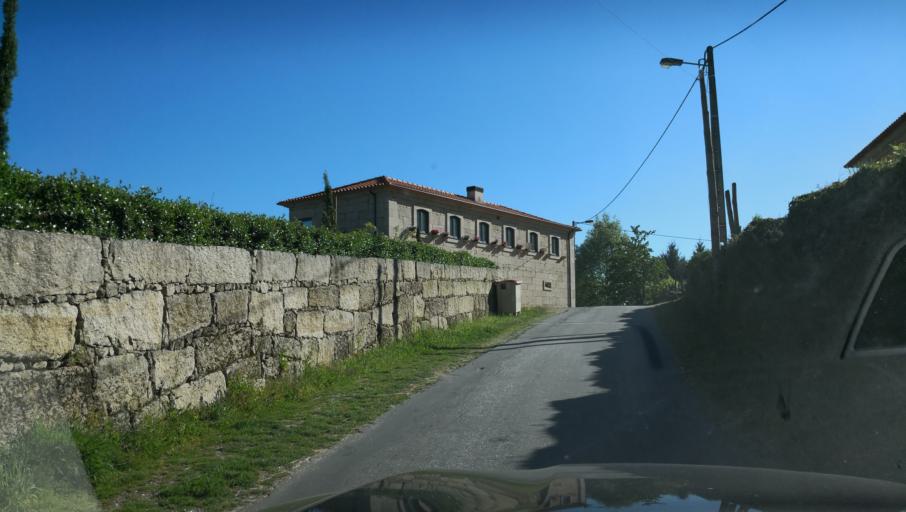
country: PT
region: Vila Real
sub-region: Vila Real
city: Vila Real
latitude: 41.3369
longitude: -7.7386
